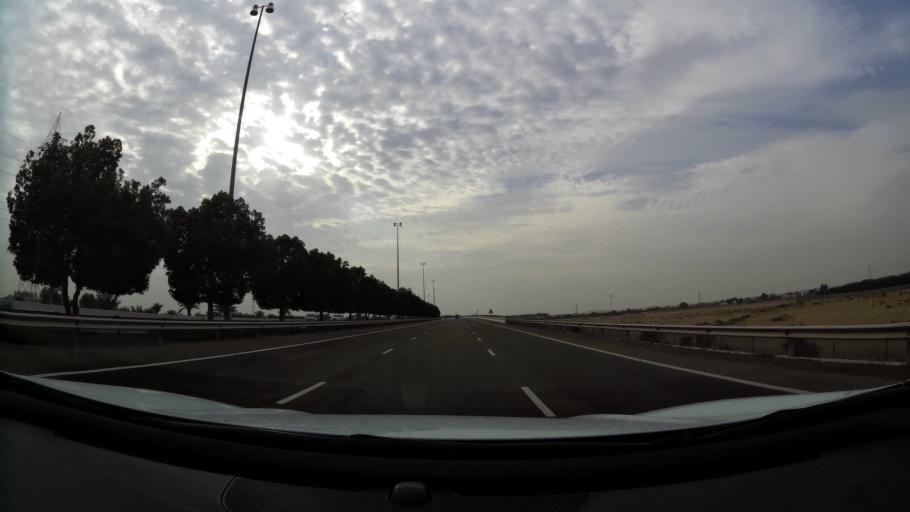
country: AE
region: Abu Dhabi
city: Abu Dhabi
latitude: 24.1849
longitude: 55.0307
